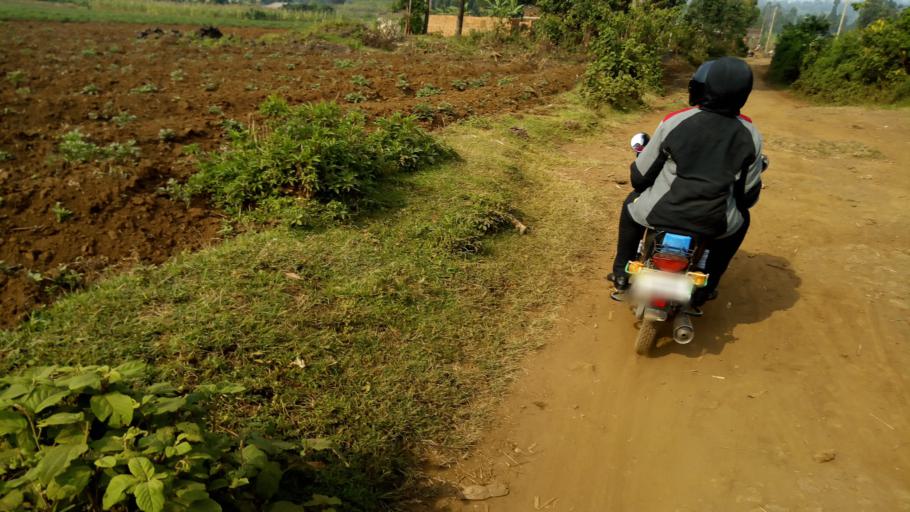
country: UG
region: Western Region
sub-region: Kisoro District
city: Kisoro
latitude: -1.3090
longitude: 29.6585
